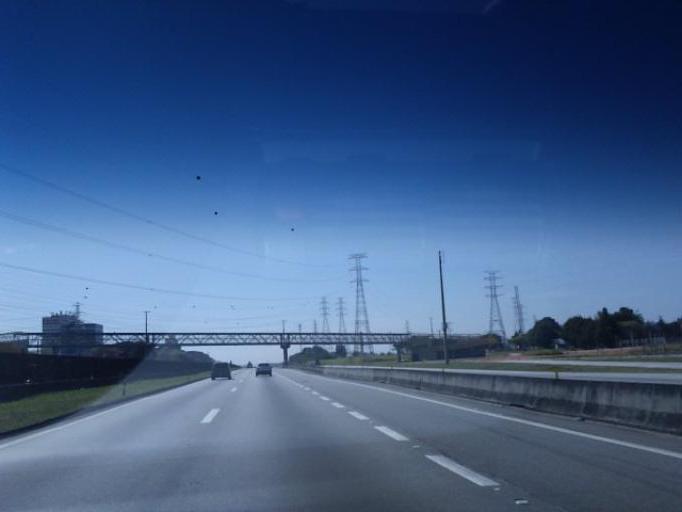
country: BR
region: Sao Paulo
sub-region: Sao Jose Dos Campos
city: Sao Jose dos Campos
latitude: -23.1867
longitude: -45.8544
